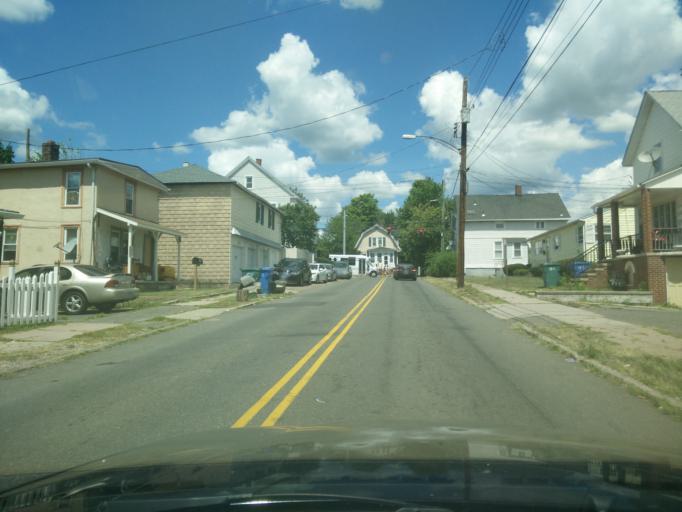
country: US
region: Connecticut
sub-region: New Haven County
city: New Haven
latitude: 41.3377
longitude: -72.9379
